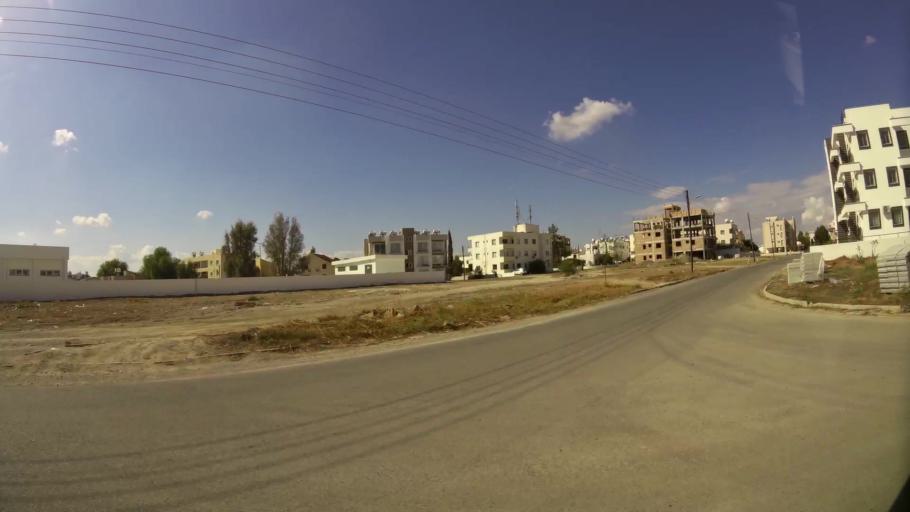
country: CY
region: Lefkosia
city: Nicosia
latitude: 35.2108
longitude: 33.3330
